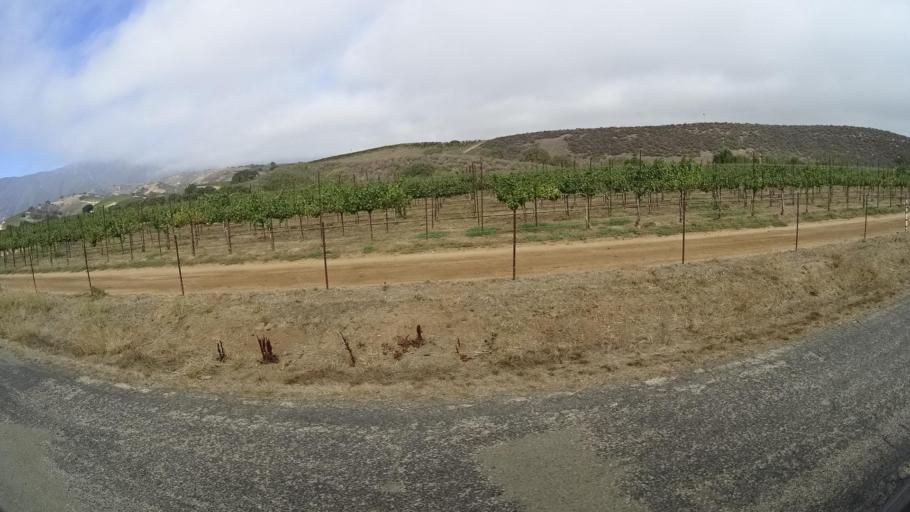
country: US
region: California
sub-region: Monterey County
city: Soledad
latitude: 36.3474
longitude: -121.3383
